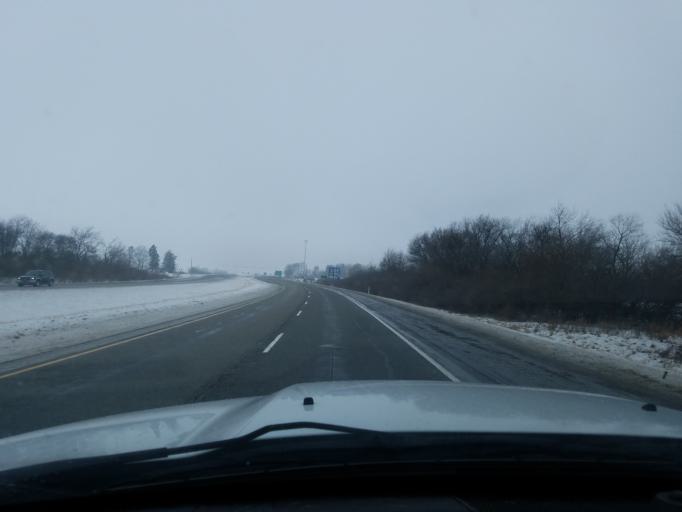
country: US
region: Indiana
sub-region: Fulton County
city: Rochester
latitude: 41.0409
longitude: -86.1984
